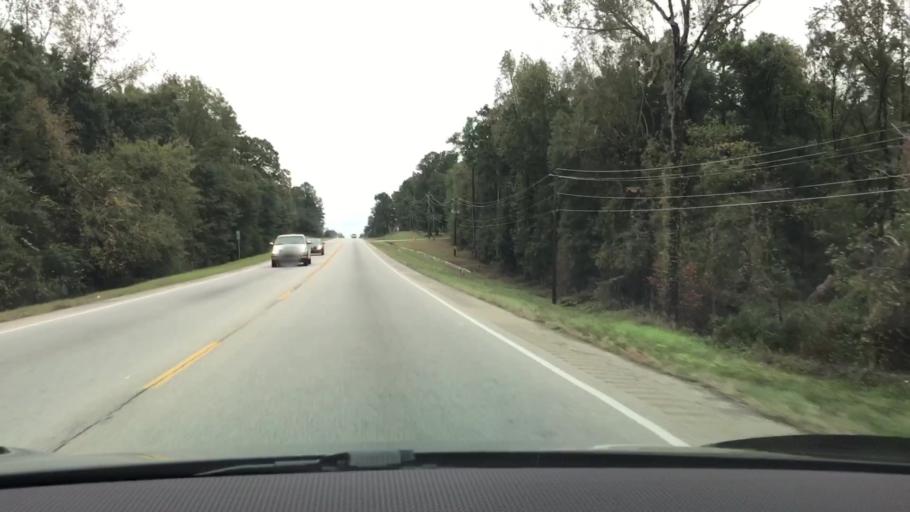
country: US
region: Georgia
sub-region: Jefferson County
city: Louisville
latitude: 33.0015
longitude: -82.3954
